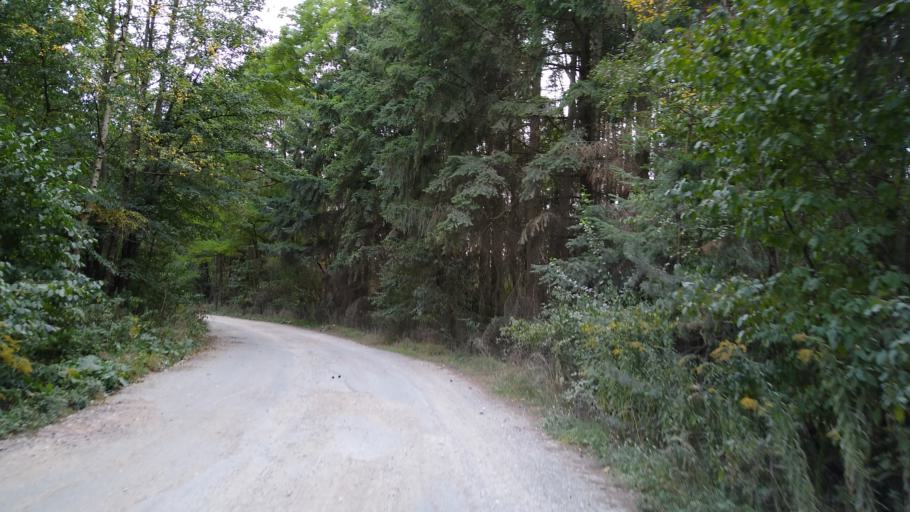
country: DE
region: Bavaria
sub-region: Regierungsbezirk Mittelfranken
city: Seukendorf
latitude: 49.4758
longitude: 10.9044
